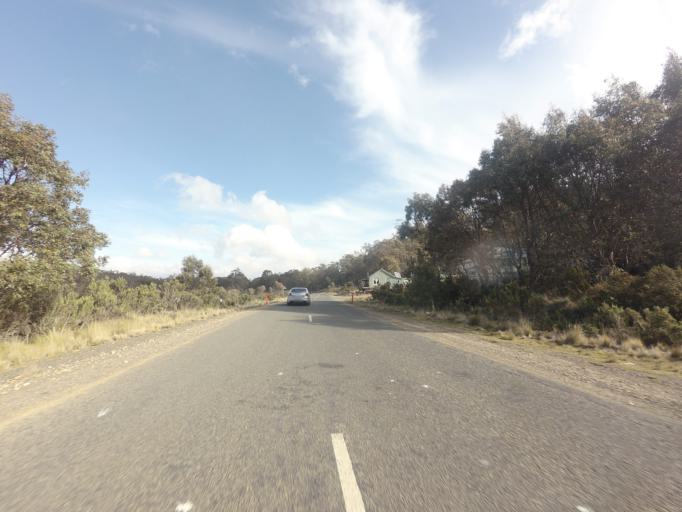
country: AU
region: Tasmania
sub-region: Meander Valley
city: Deloraine
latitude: -41.7830
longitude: 146.7052
